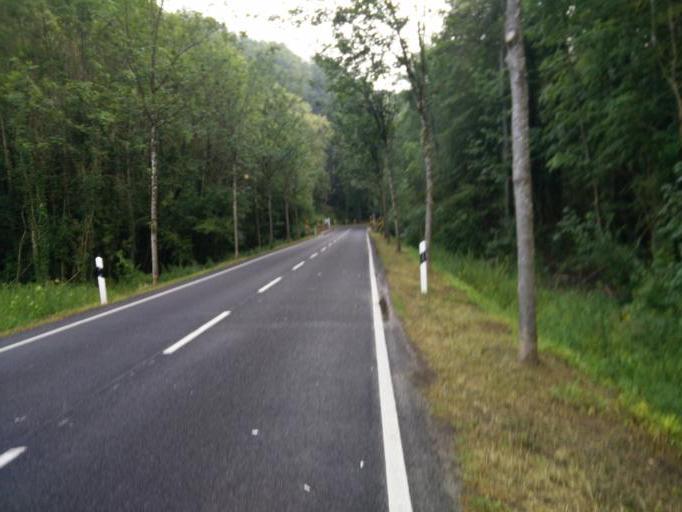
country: LU
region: Luxembourg
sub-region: Canton de Capellen
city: Mamer
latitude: 49.6412
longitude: 6.0482
